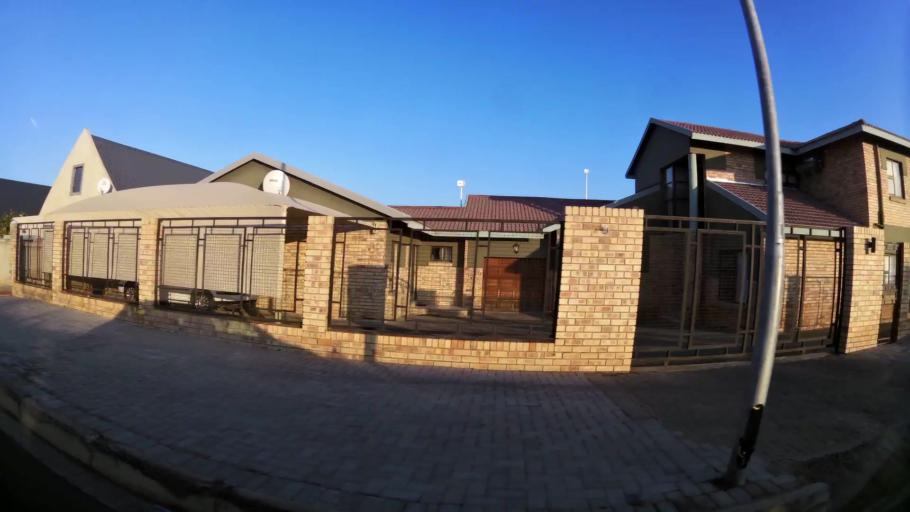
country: ZA
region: Orange Free State
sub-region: Mangaung Metropolitan Municipality
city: Bloemfontein
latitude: -29.0952
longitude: 26.1656
